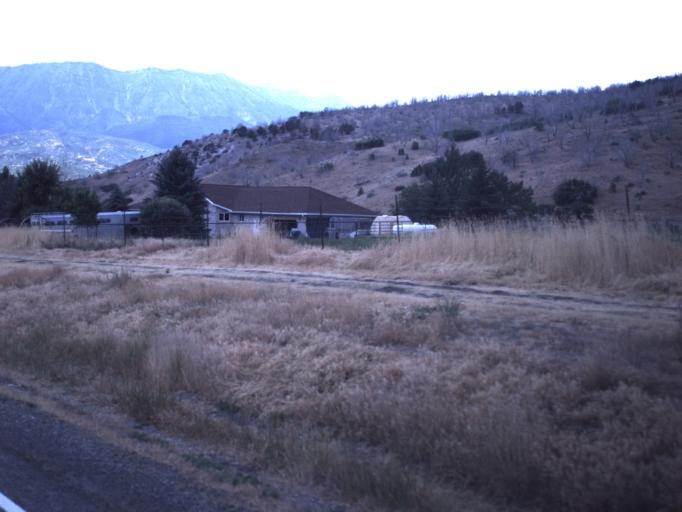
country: US
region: Utah
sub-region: Sanpete County
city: Fountain Green
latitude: 39.7080
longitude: -111.7144
